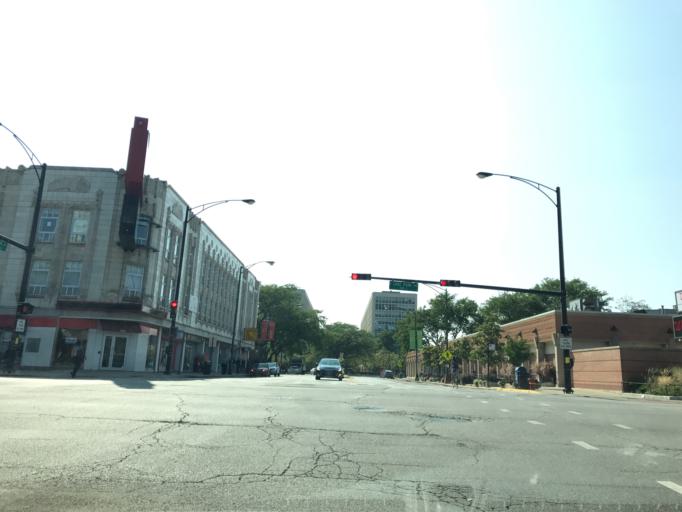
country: US
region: Illinois
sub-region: Cook County
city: Chicago
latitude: 41.7952
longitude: -87.5872
